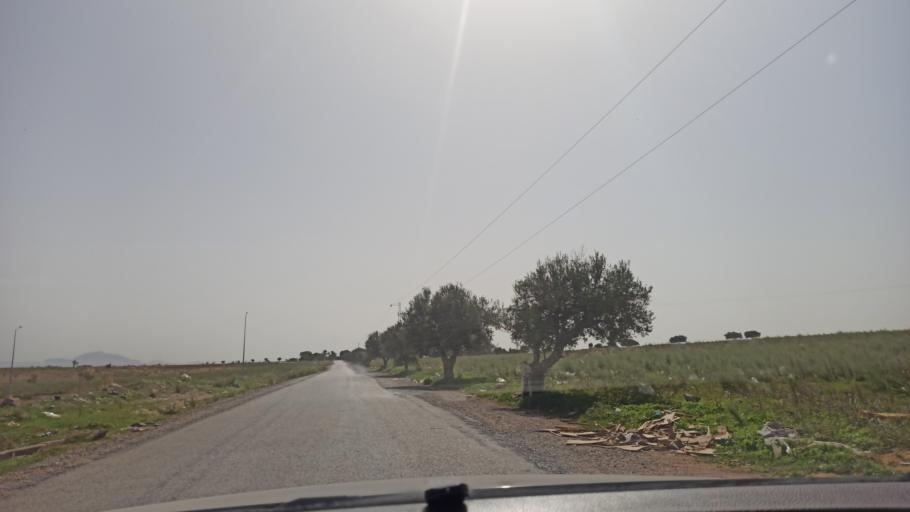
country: TN
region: Manouba
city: Manouba
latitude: 36.7361
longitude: 10.0846
